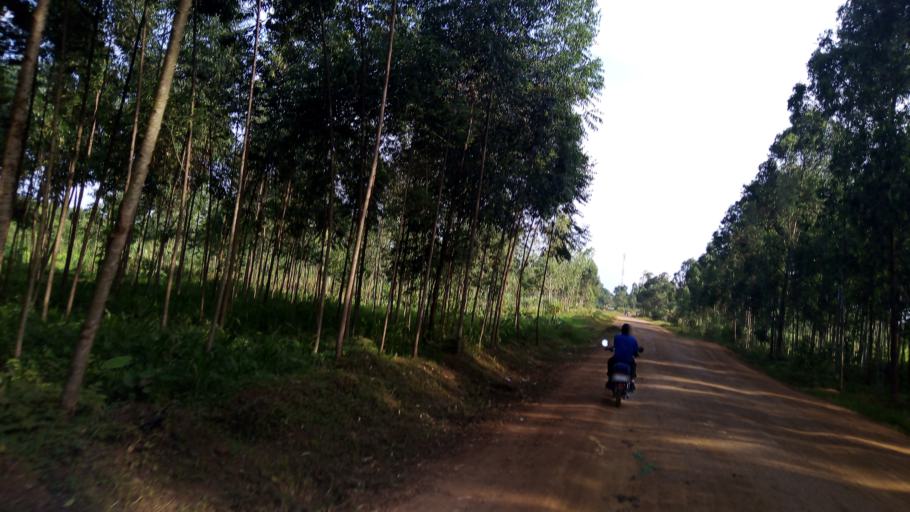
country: UG
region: Eastern Region
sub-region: Mbale District
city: Mbale
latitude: 1.0672
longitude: 34.1557
